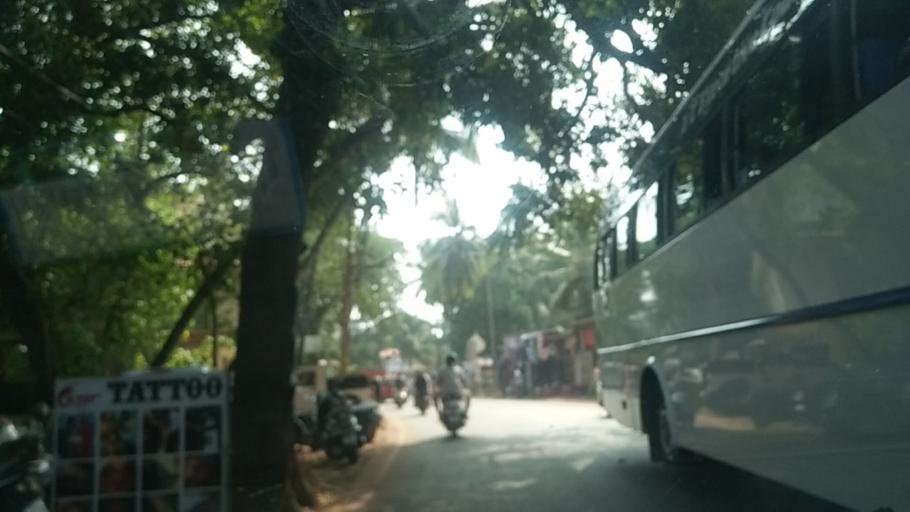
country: IN
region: Goa
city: Calangute
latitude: 15.5415
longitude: 73.7649
